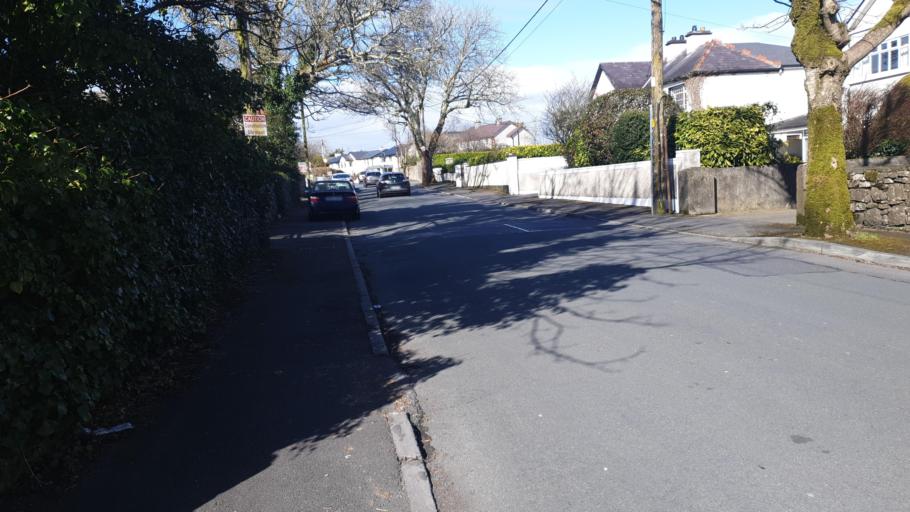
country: IE
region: Connaught
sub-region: County Galway
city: Gaillimh
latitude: 53.2698
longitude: -9.0718
